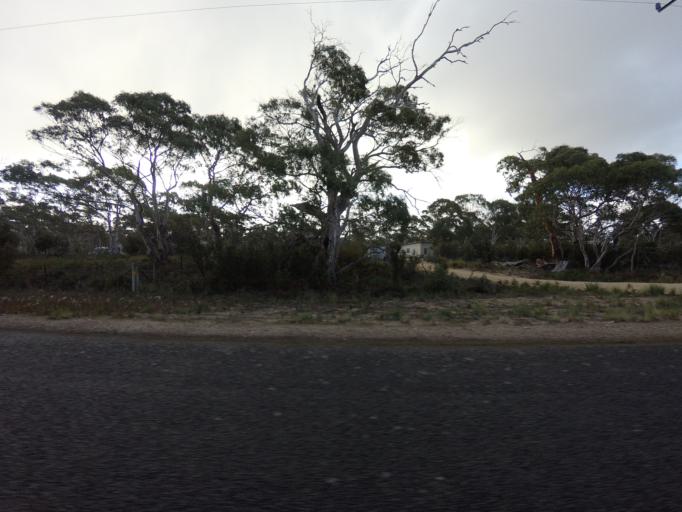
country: AU
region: Tasmania
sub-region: Break O'Day
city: St Helens
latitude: -42.0999
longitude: 148.0861
